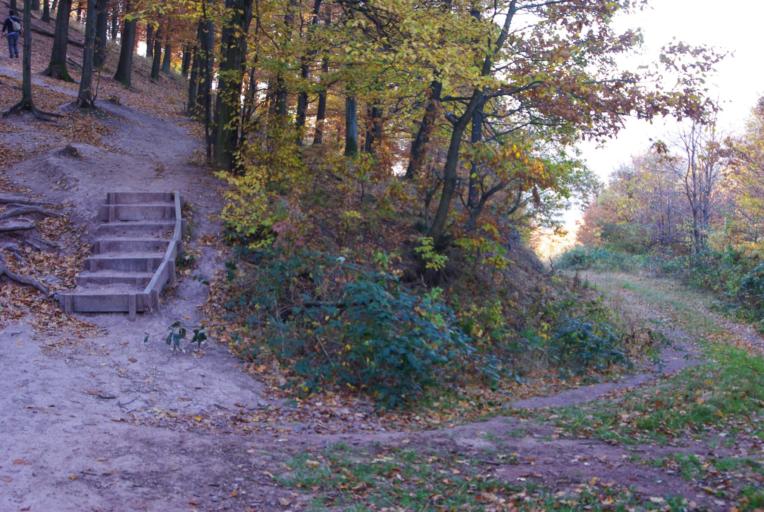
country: HU
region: Komarom-Esztergom
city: Pilismarot
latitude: 47.7444
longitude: 18.9072
